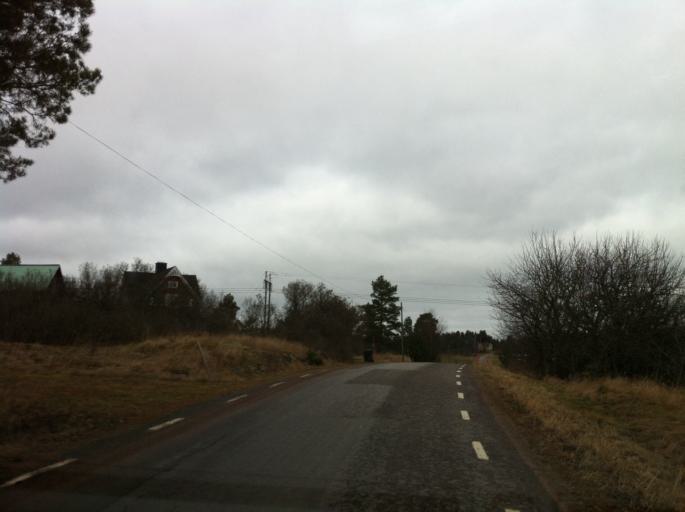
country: SE
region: Kalmar
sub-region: Vasterviks Kommun
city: Overum
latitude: 57.9101
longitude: 16.1185
